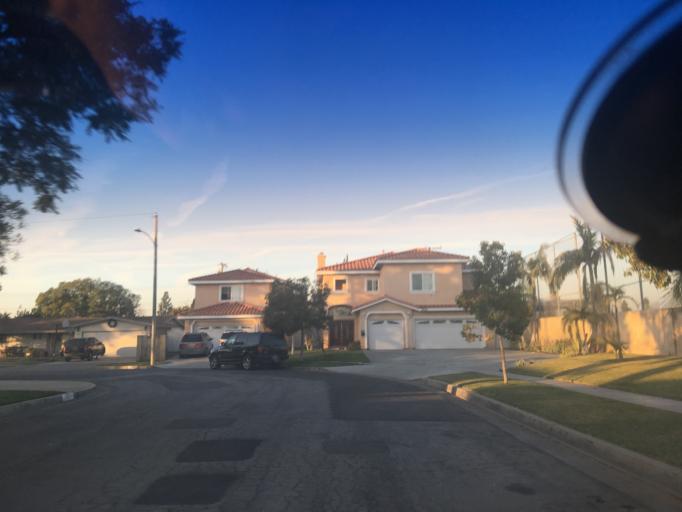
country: US
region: California
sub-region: Orange County
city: Anaheim
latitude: 33.8219
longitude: -117.8872
